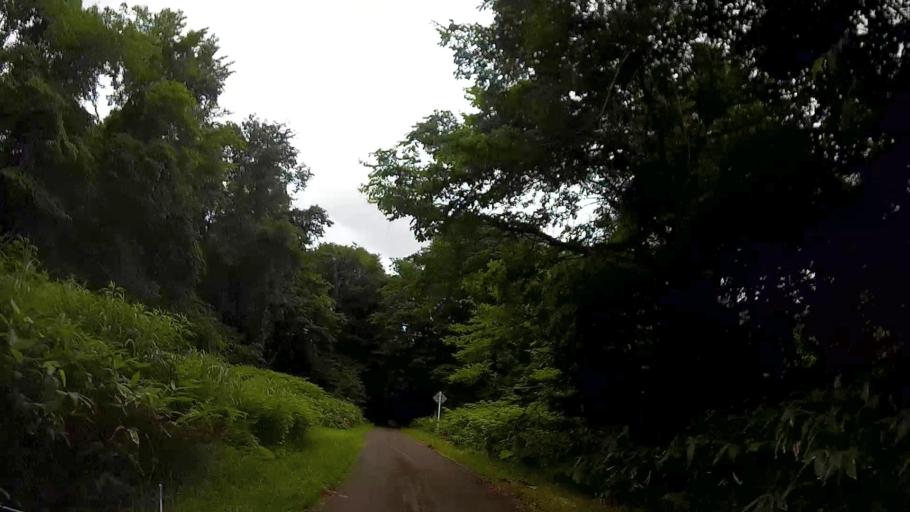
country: JP
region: Hokkaido
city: Nanae
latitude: 42.0482
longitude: 140.4902
